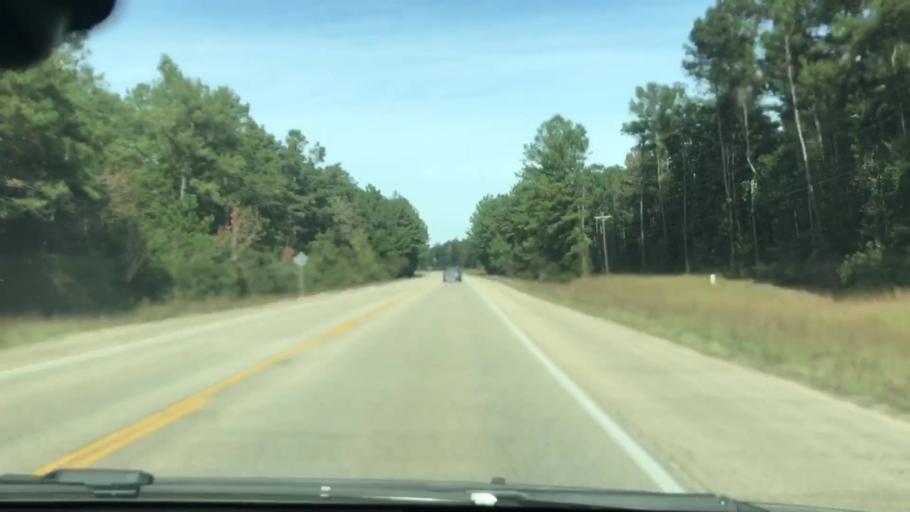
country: US
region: Louisiana
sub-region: Saint Tammany Parish
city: Pearl River
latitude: 30.4749
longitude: -89.8120
